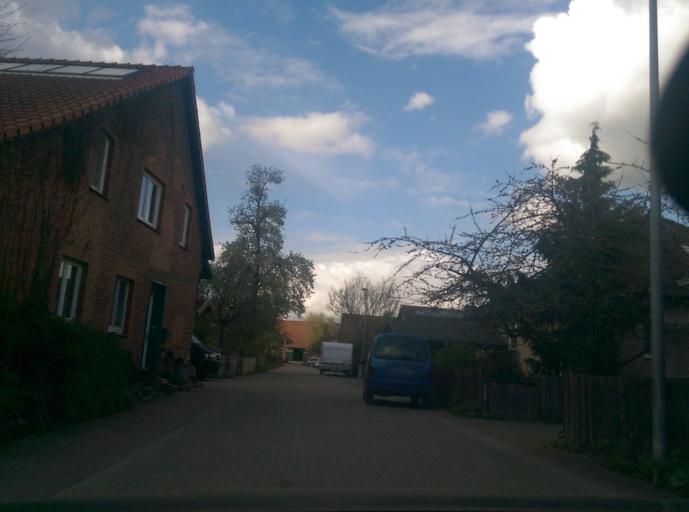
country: DE
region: Lower Saxony
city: Lindwedel
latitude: 52.5527
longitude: 9.6789
